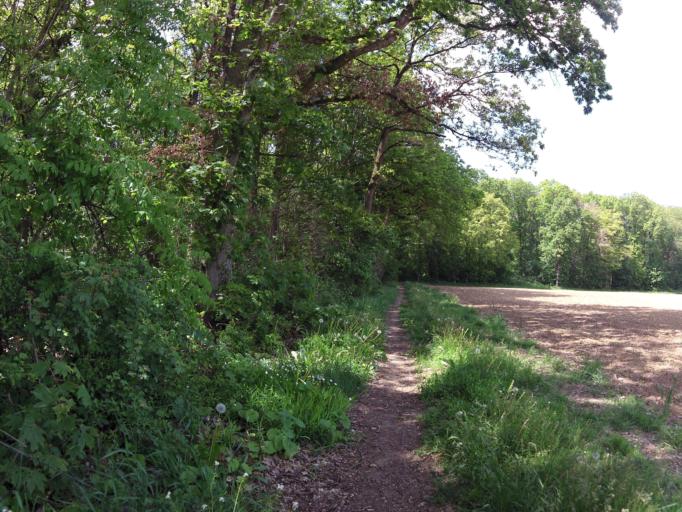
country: DE
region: Bavaria
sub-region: Regierungsbezirk Unterfranken
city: Theilheim
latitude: 49.7438
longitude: 10.0368
